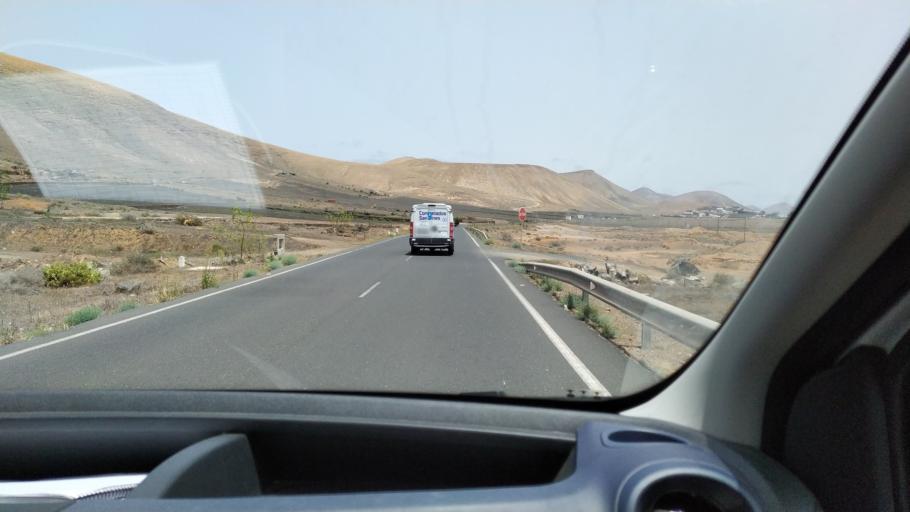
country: ES
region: Canary Islands
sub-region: Provincia de Las Palmas
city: Yaiza
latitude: 28.9236
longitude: -13.7656
